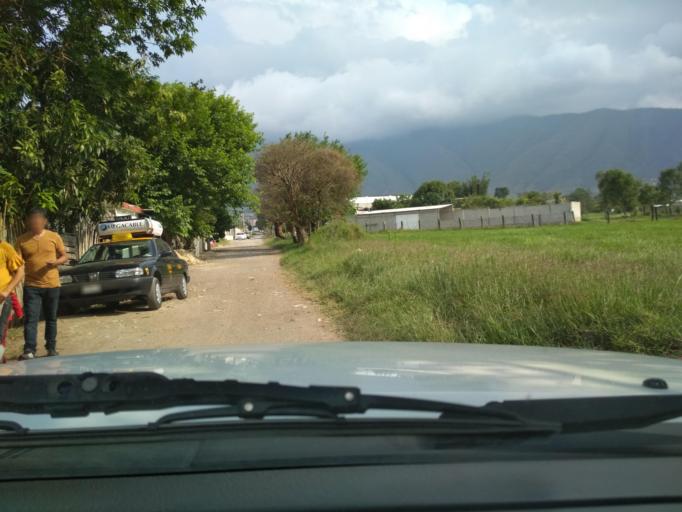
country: MX
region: Veracruz
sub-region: Acultzingo
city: Acatla
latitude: 18.7680
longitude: -97.2249
